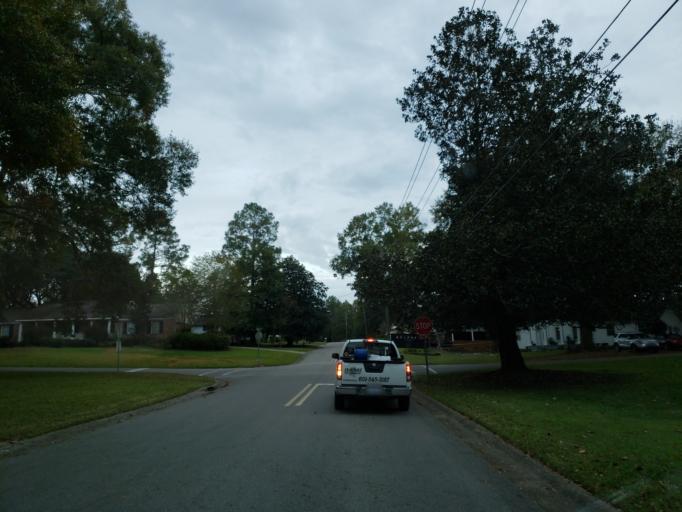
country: US
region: Mississippi
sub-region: Lamar County
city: West Hattiesburg
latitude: 31.3146
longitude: -89.3349
